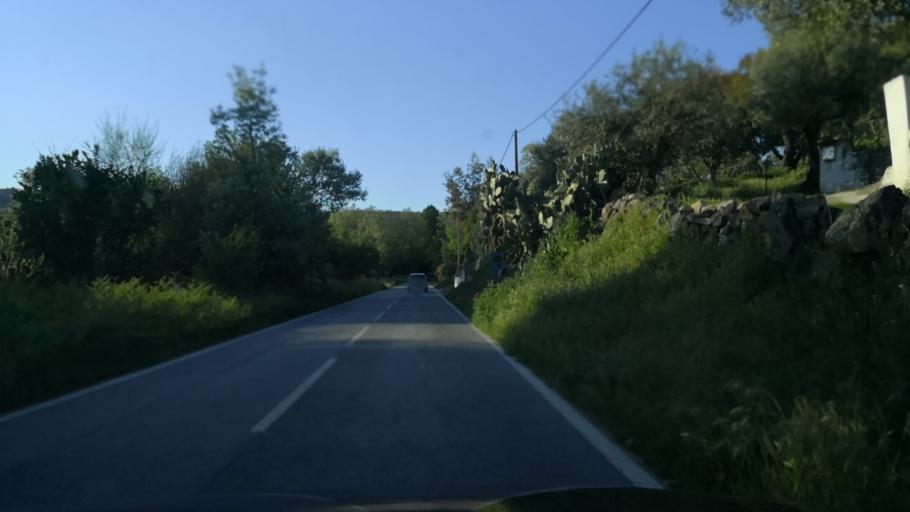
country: PT
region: Portalegre
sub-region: Marvao
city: Marvao
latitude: 39.3610
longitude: -7.4037
